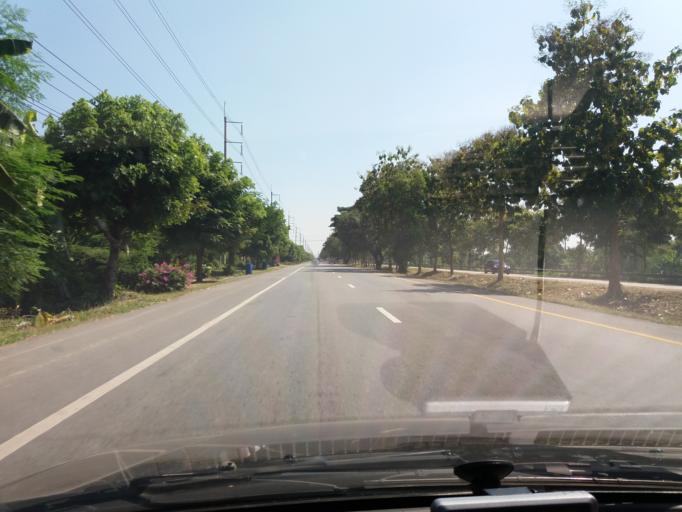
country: TH
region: Chai Nat
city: Sankhaburi
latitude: 15.0788
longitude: 100.1428
